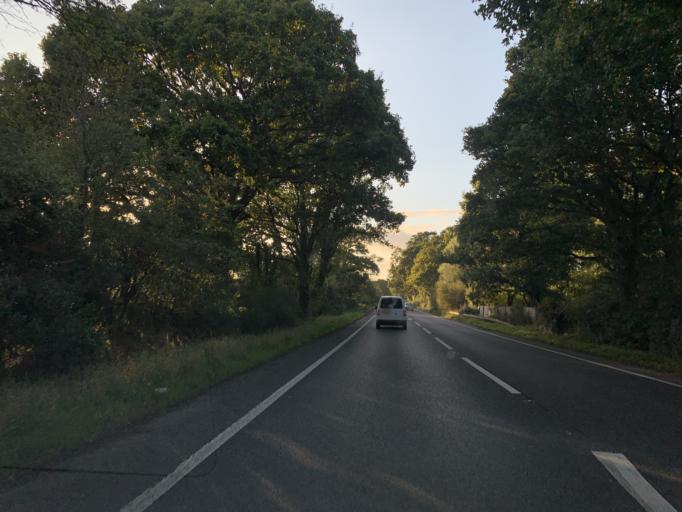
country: GB
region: England
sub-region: Hampshire
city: West Wellow
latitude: 50.9747
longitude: -1.6182
